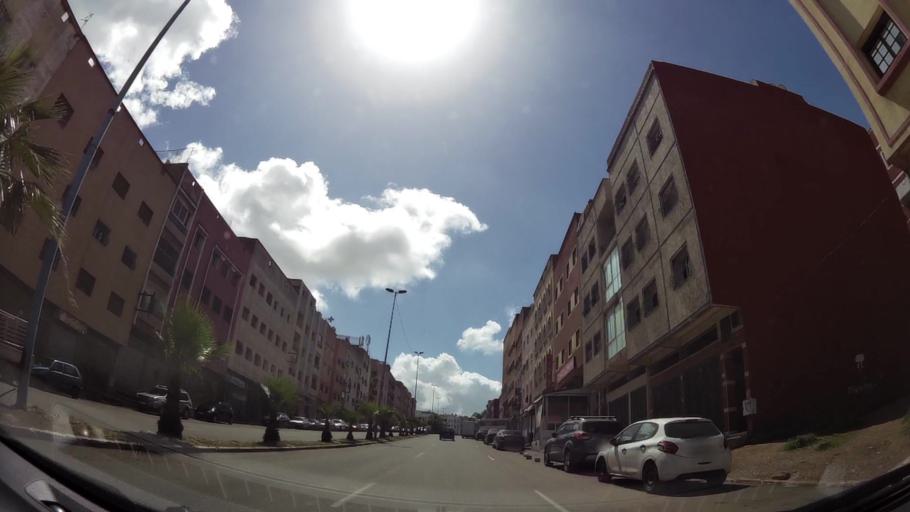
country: MA
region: Grand Casablanca
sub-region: Casablanca
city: Casablanca
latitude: 33.5347
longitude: -7.5860
